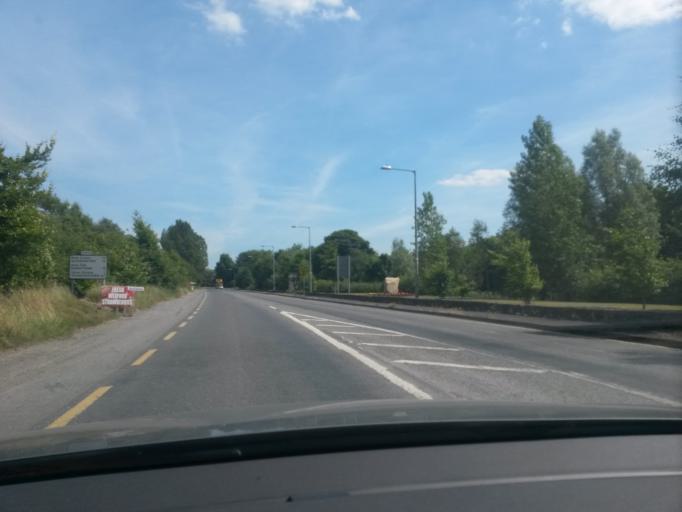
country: IE
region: Leinster
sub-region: Kildare
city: Naas
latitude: 53.2132
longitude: -6.6497
